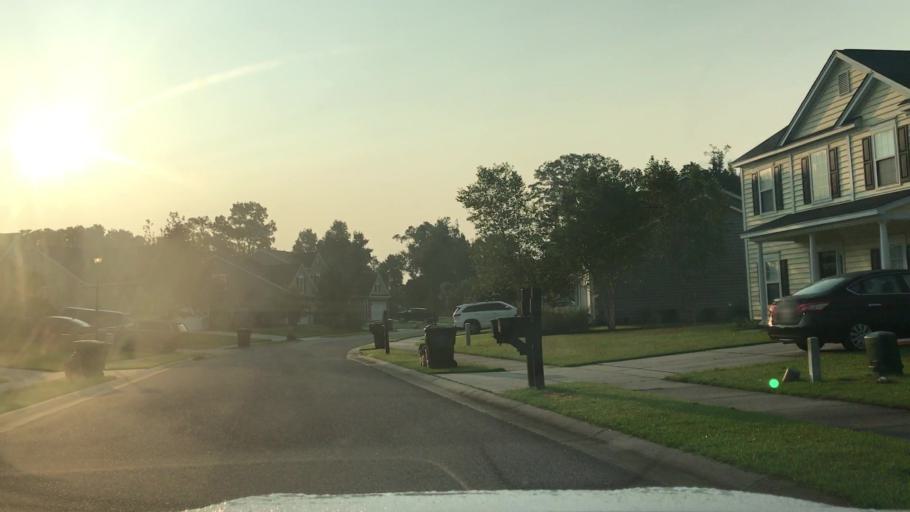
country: US
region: South Carolina
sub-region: Charleston County
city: Shell Point
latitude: 32.8375
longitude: -80.0986
